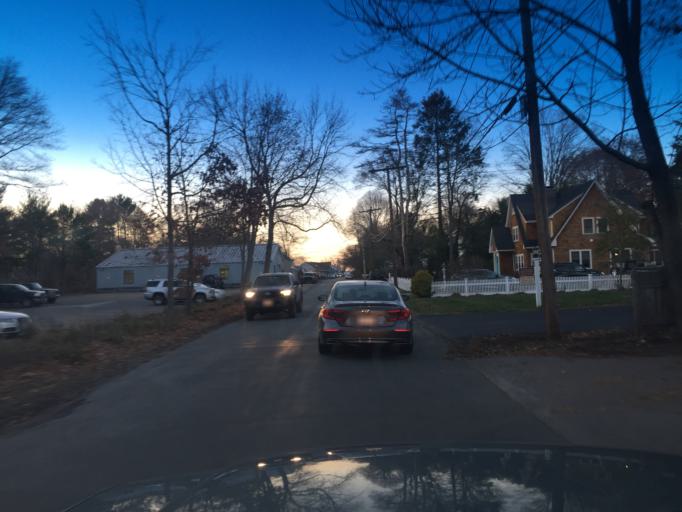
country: US
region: Massachusetts
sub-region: Norfolk County
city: Medfield
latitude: 42.1832
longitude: -71.3041
